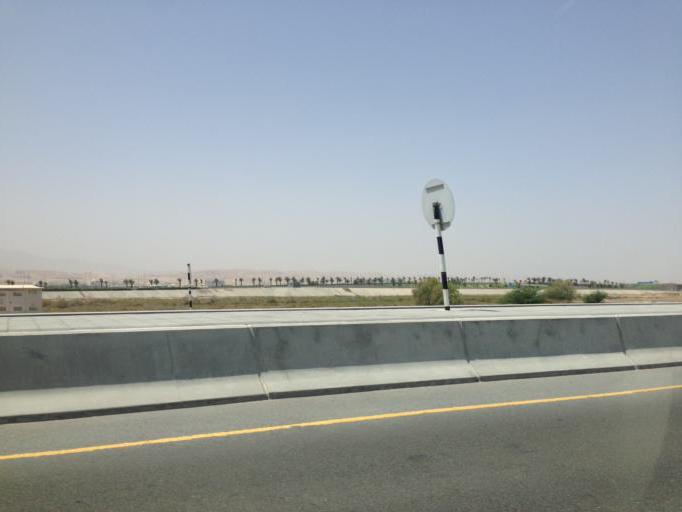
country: OM
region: Muhafazat Masqat
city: Bawshar
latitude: 23.6069
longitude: 58.3185
